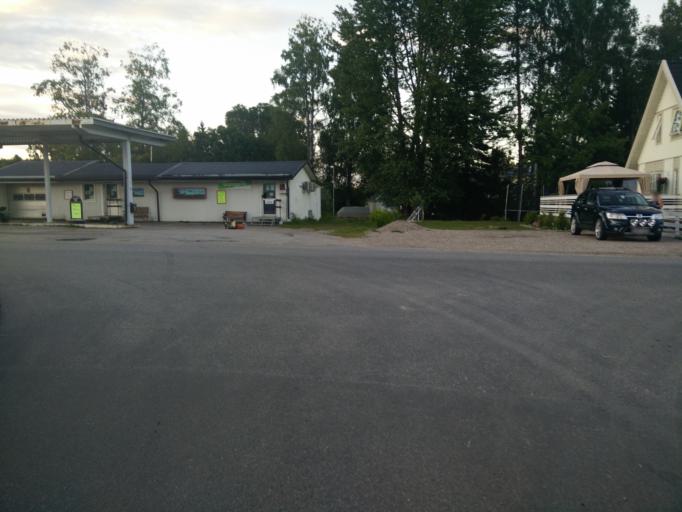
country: SE
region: Vaesternorrland
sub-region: Sundsvalls Kommun
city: Njurundabommen
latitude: 62.2692
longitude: 17.3746
